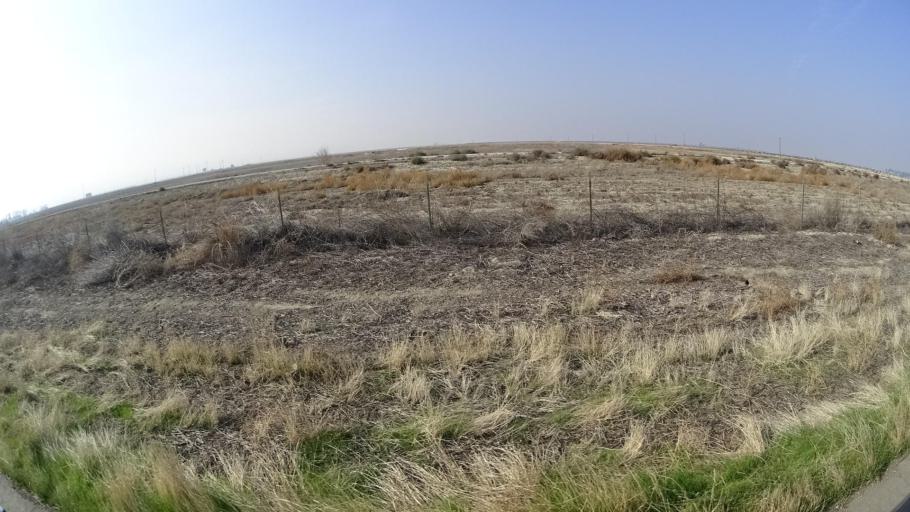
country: US
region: California
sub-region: Kern County
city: Buttonwillow
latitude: 35.3388
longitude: -119.3590
